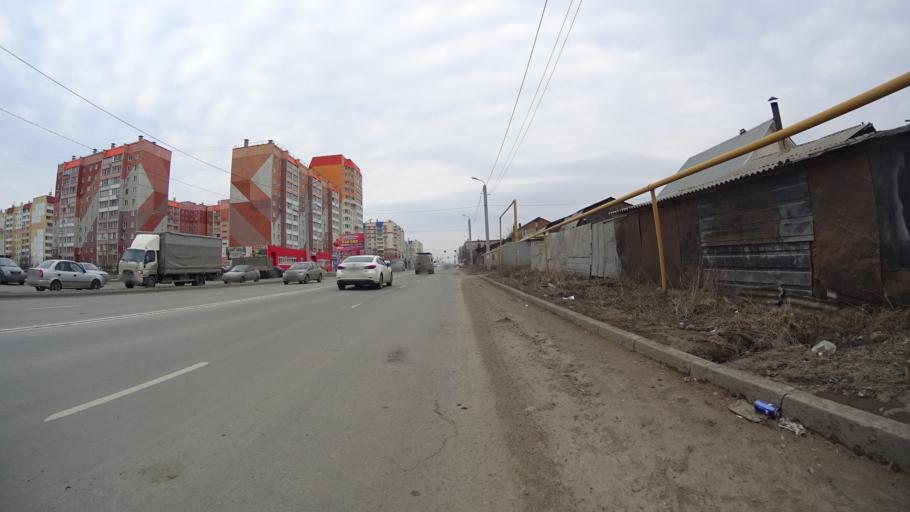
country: RU
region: Chelyabinsk
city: Zheleznodorozhnyy
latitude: 55.1678
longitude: 61.5253
